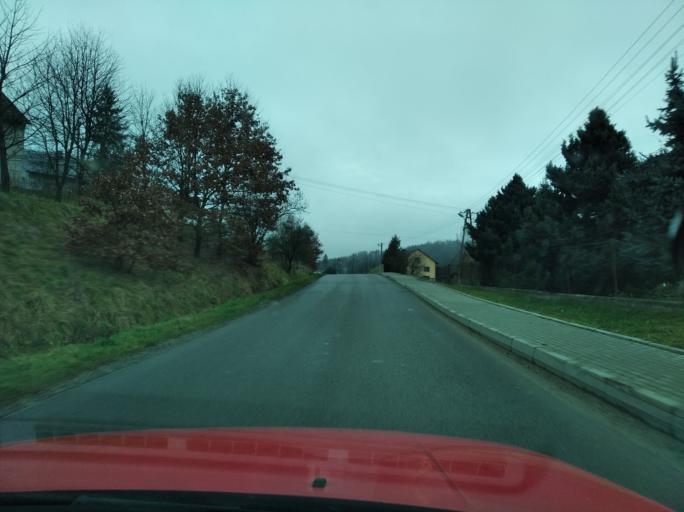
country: PL
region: Subcarpathian Voivodeship
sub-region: Powiat przemyski
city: Nienadowa
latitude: 49.8447
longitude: 22.4314
